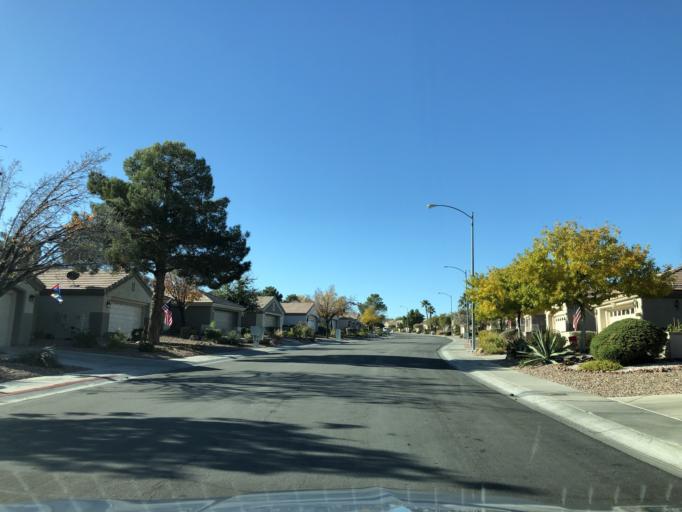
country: US
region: Nevada
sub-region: Clark County
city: Whitney
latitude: 36.0115
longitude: -115.0739
